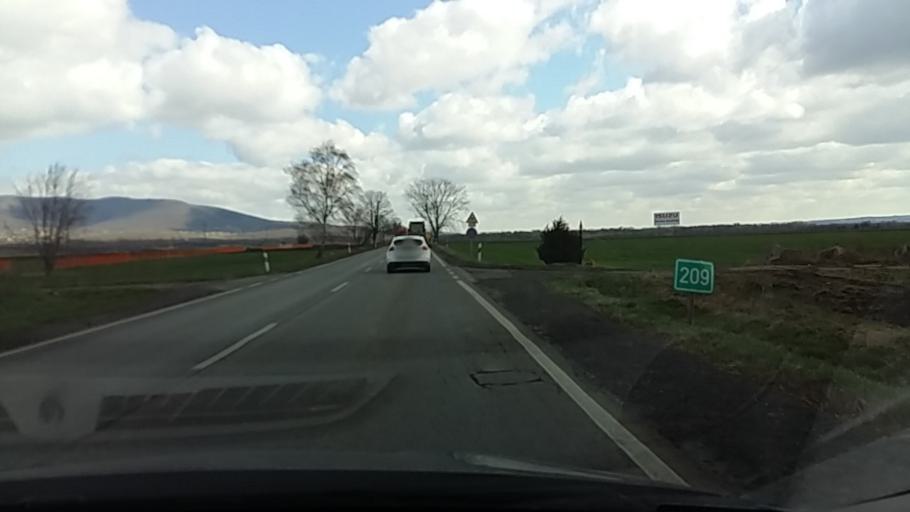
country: HU
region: Baranya
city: Pellerd
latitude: 46.0539
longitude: 18.0845
